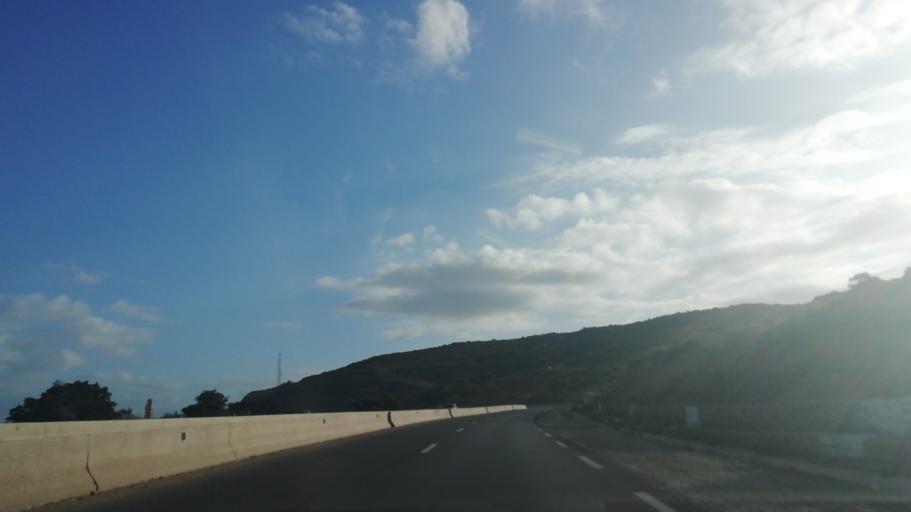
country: DZ
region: Mostaganem
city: Mostaganem
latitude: 36.1088
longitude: 0.2224
